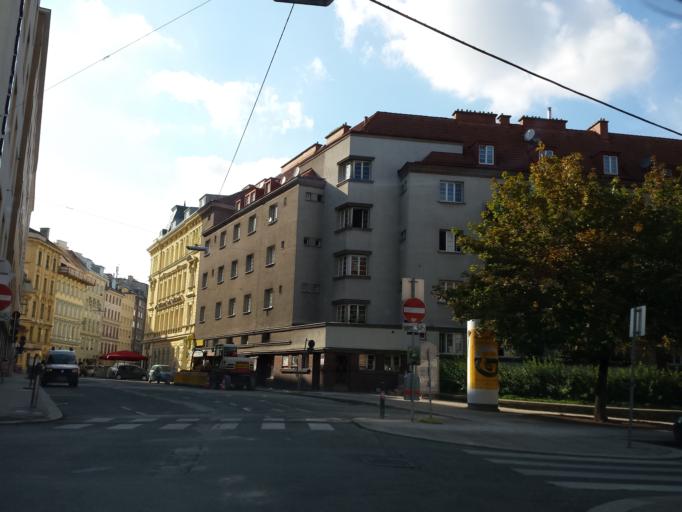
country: AT
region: Vienna
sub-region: Wien Stadt
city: Vienna
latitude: 48.1956
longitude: 16.3992
